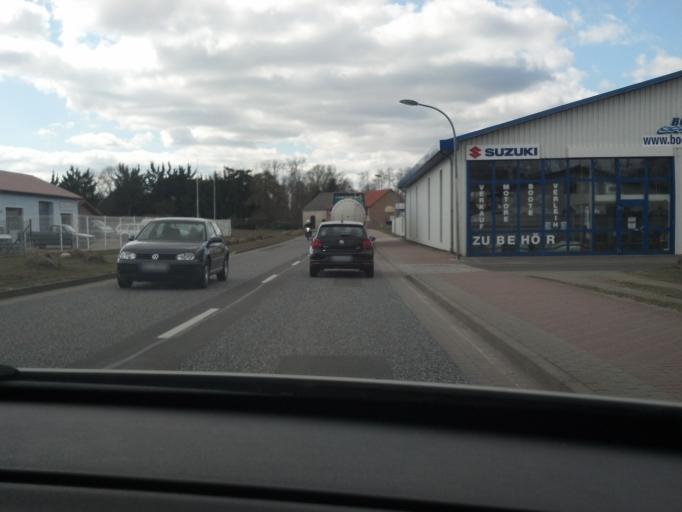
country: DE
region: Mecklenburg-Vorpommern
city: Wesenberg
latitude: 53.2801
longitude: 12.9817
